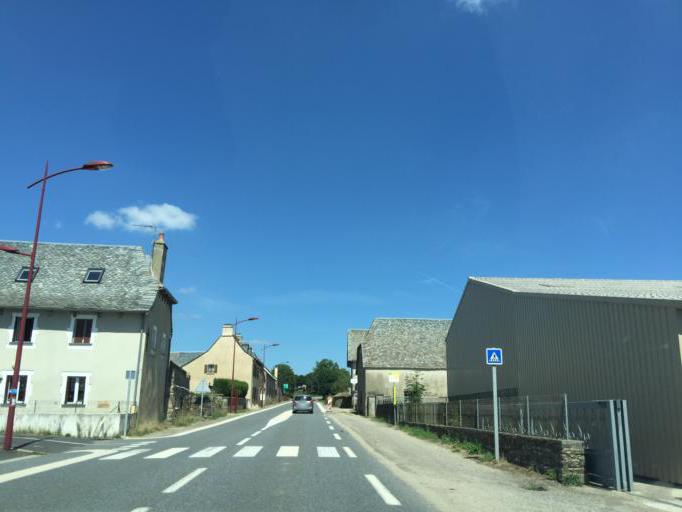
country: FR
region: Midi-Pyrenees
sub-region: Departement de l'Aveyron
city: Laguiole
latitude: 44.6113
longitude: 2.8063
